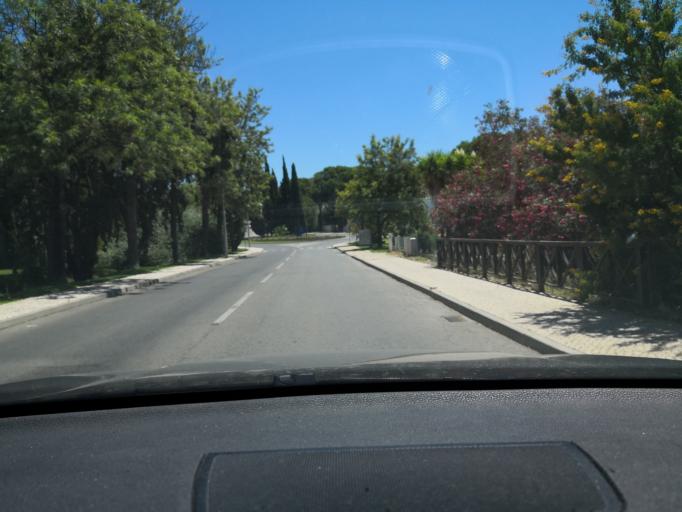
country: PT
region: Faro
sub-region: Loule
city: Vilamoura
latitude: 37.1039
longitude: -8.1193
